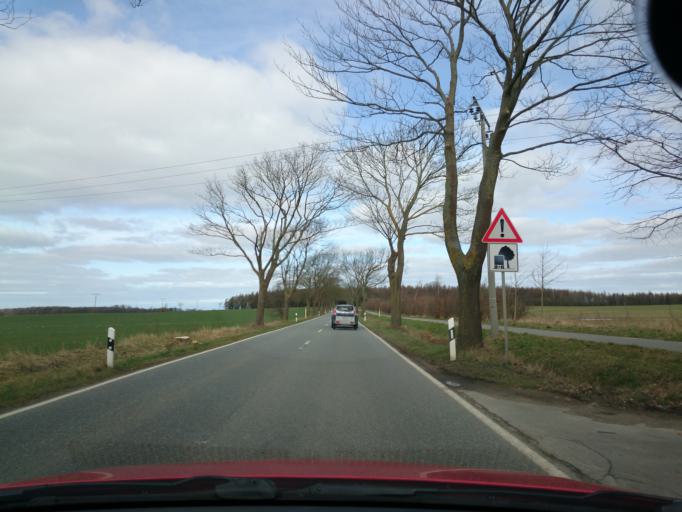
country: DE
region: Mecklenburg-Vorpommern
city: Velgast
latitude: 54.2798
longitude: 12.8024
